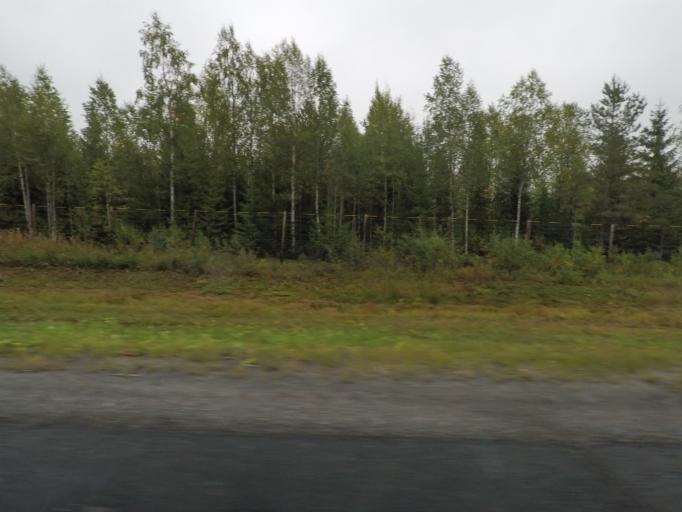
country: FI
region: Northern Savo
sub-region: Kuopio
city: Kuopio
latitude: 62.7868
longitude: 27.5940
